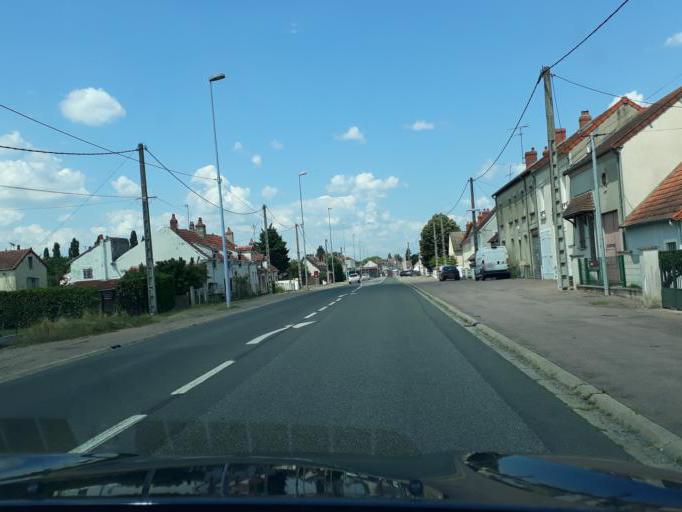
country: FR
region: Bourgogne
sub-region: Departement de la Nievre
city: Challuy
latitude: 46.9668
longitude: 3.1569
